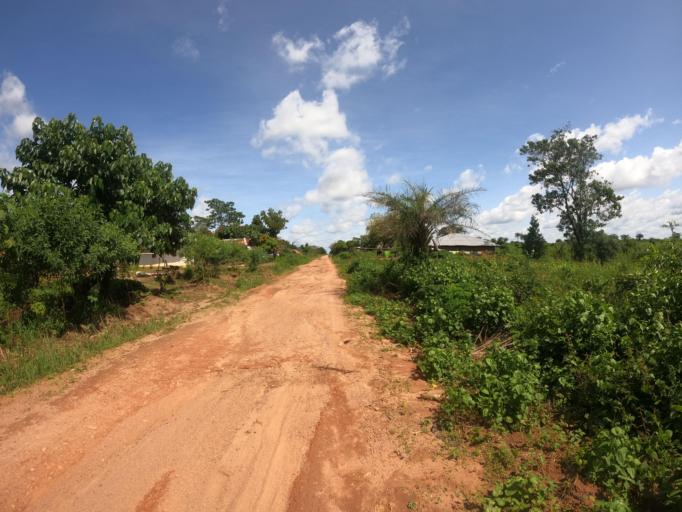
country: SL
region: Northern Province
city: Masingbi
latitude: 8.8322
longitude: -11.9935
